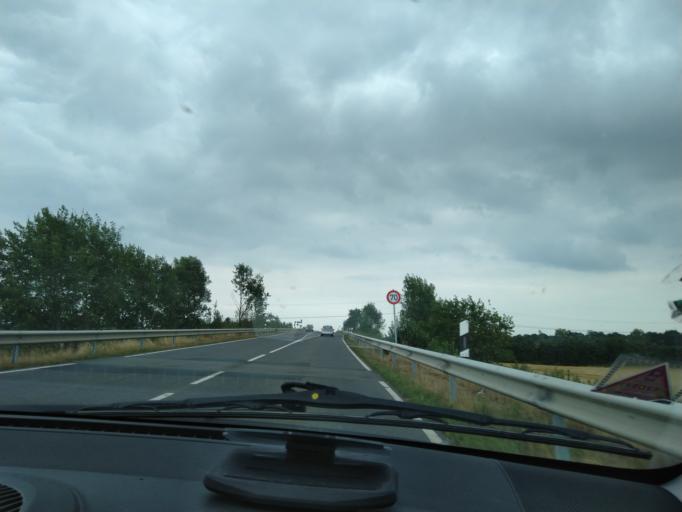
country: DE
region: Lower Saxony
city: Rhede
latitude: 53.0663
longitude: 7.2341
